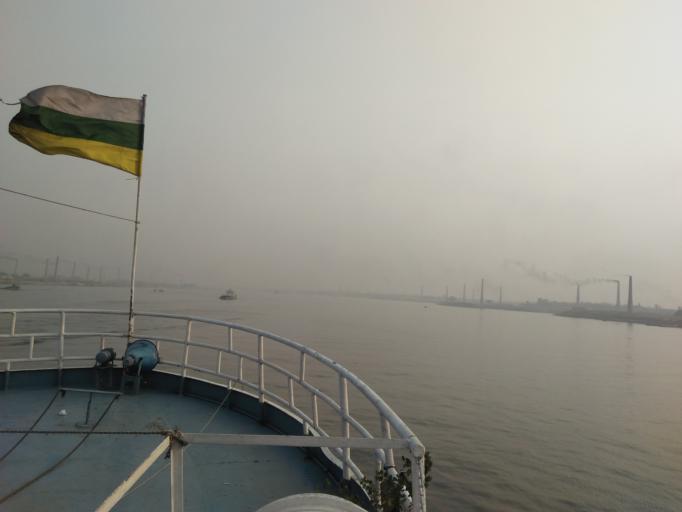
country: BD
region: Dhaka
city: Narayanganj
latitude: 23.6216
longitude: 90.4537
